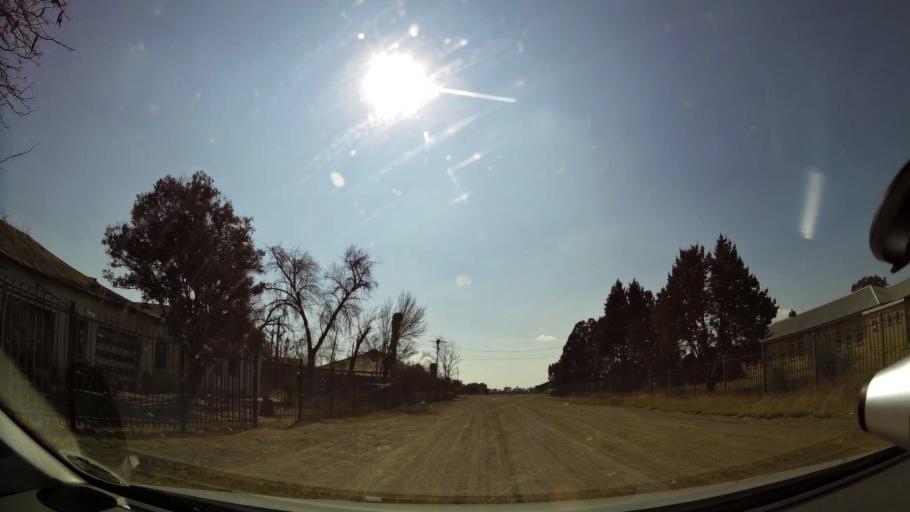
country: ZA
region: Orange Free State
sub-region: Mangaung Metropolitan Municipality
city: Bloemfontein
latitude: -29.1583
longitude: 26.3152
